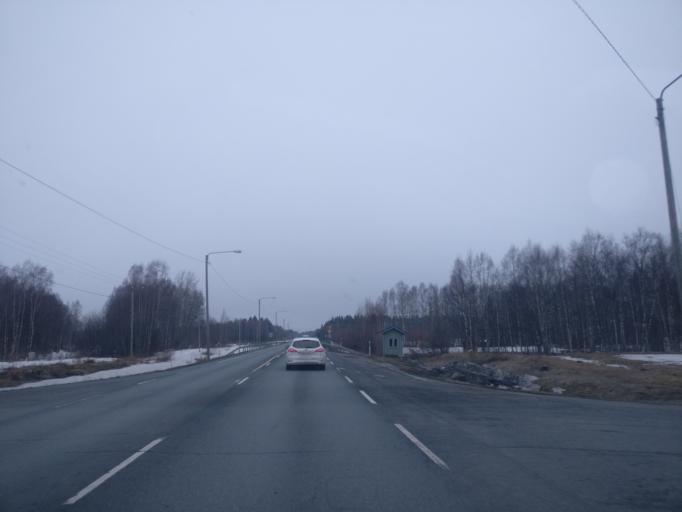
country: FI
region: Lapland
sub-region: Kemi-Tornio
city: Simo
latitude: 65.6697
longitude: 24.9270
